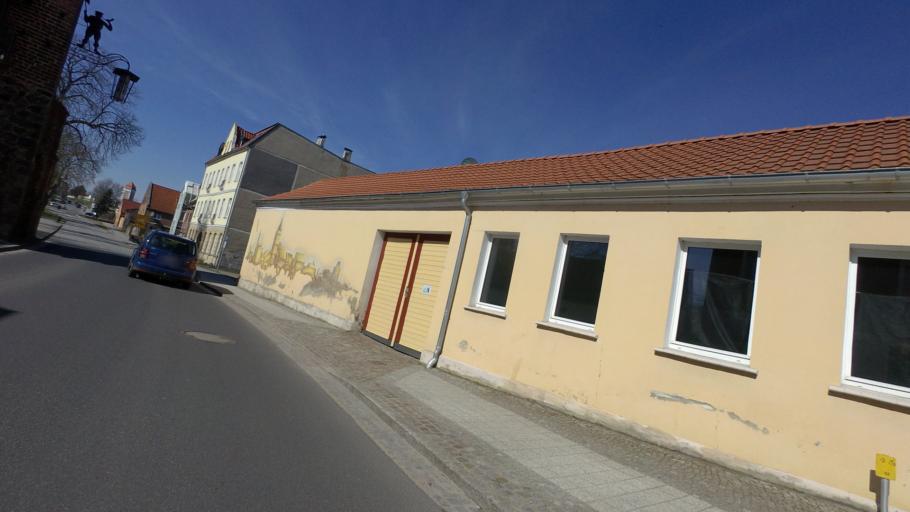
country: DE
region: Brandenburg
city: Muncheberg
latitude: 52.5046
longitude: 14.1383
